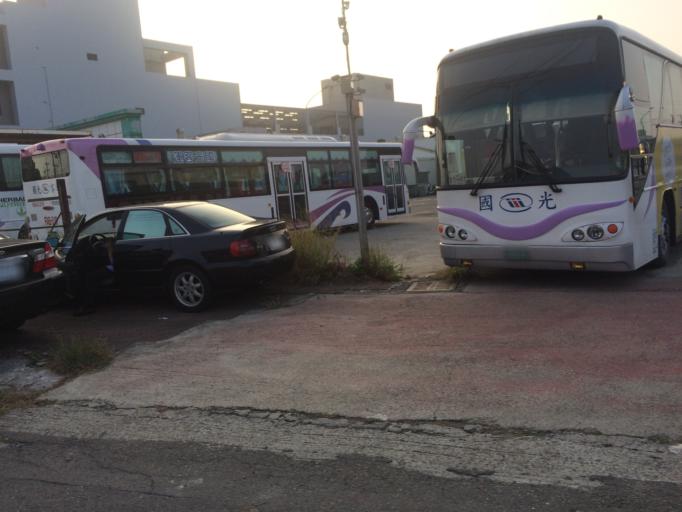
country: TW
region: Taiwan
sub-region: Hsinchu
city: Hsinchu
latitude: 24.7823
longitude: 120.9193
